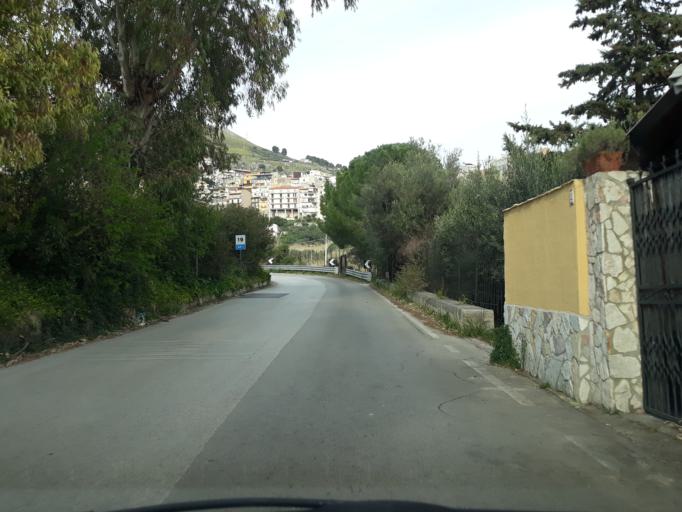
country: IT
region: Sicily
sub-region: Palermo
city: Montelepre
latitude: 38.0874
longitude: 13.1662
